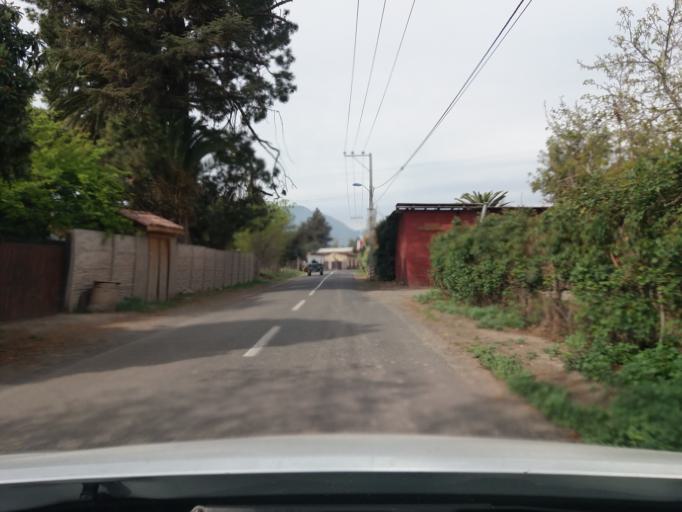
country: CL
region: Valparaiso
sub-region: Provincia de Los Andes
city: Los Andes
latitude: -32.8355
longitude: -70.6602
